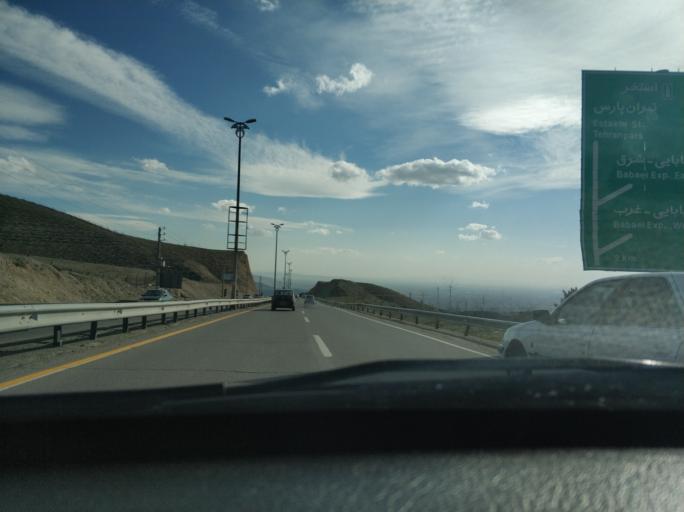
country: IR
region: Tehran
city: Tajrish
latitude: 35.7918
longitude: 51.5690
